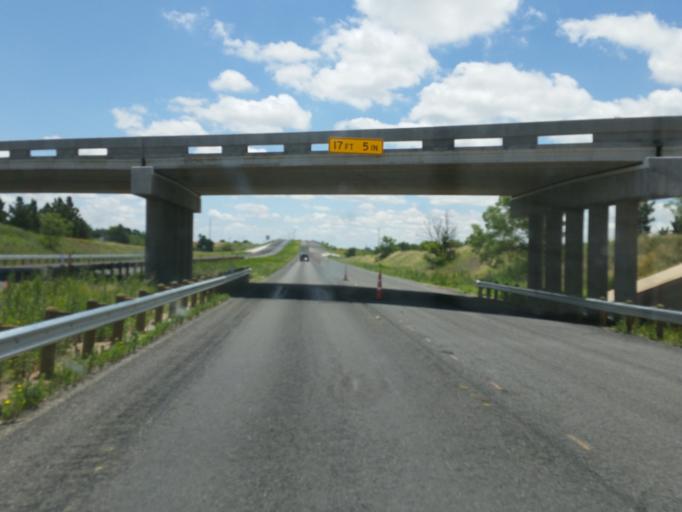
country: US
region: Texas
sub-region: Scurry County
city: Snyder
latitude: 32.7049
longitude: -100.8684
